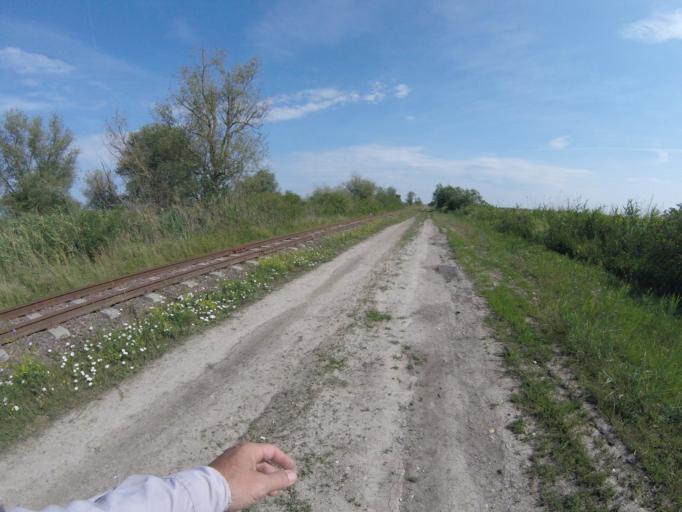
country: HU
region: Hajdu-Bihar
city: Hortobagy
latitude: 47.6416
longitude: 21.0859
